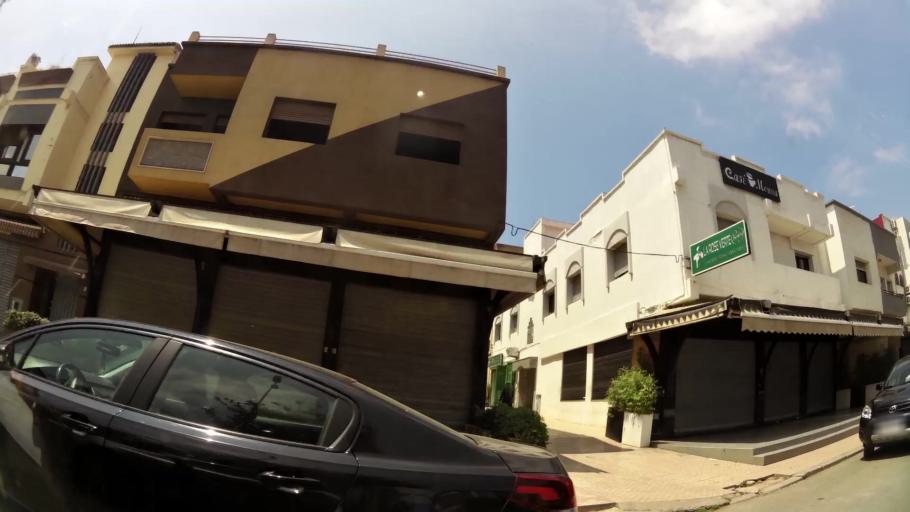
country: MA
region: Rabat-Sale-Zemmour-Zaer
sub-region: Skhirate-Temara
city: Temara
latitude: 33.9726
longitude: -6.8923
